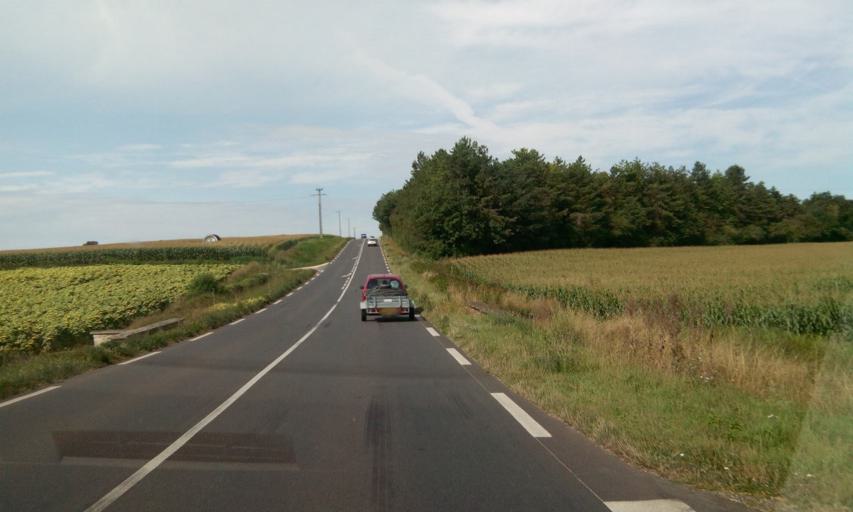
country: FR
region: Poitou-Charentes
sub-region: Departement de la Vienne
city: Chaunay
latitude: 46.1411
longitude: 0.2041
